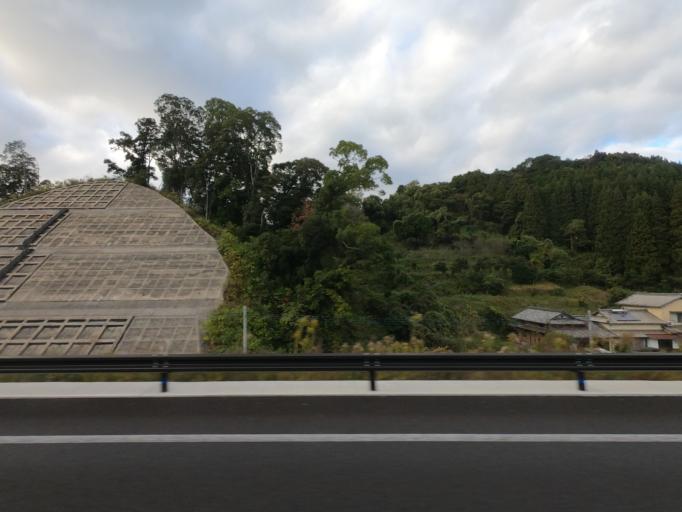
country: JP
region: Kumamoto
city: Minamata
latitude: 32.2272
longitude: 130.4375
